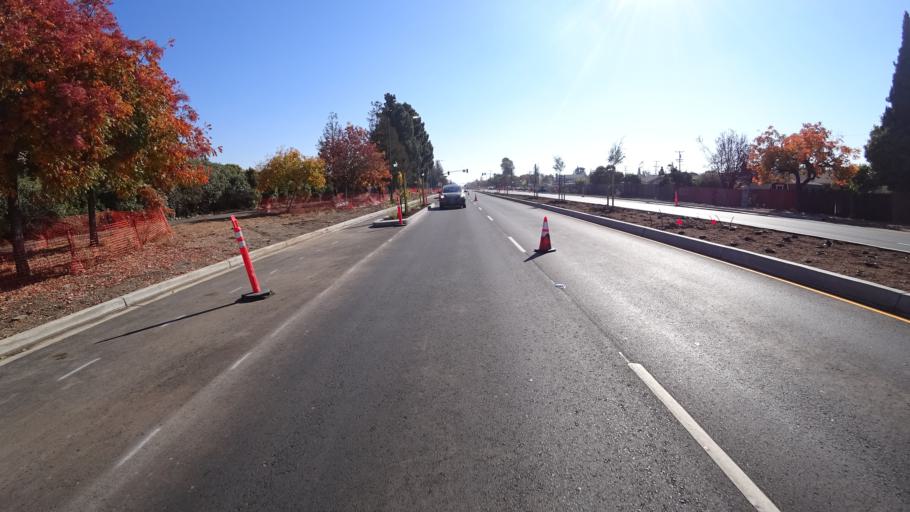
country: US
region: California
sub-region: Alameda County
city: Union City
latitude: 37.6155
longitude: -122.0306
